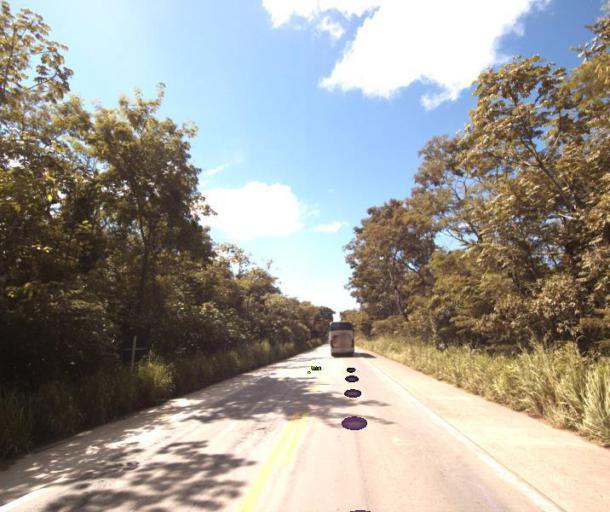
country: BR
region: Goias
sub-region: Uruana
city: Uruana
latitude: -15.5266
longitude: -49.4608
